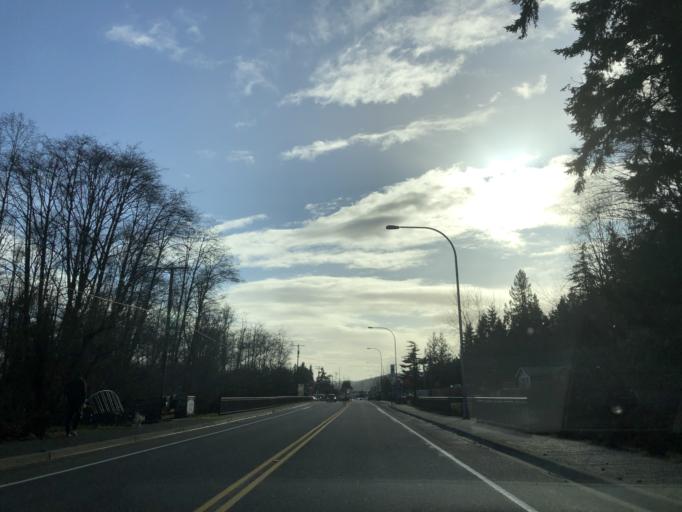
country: US
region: Washington
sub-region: Kitsap County
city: Poulsbo
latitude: 47.7512
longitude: -122.6540
